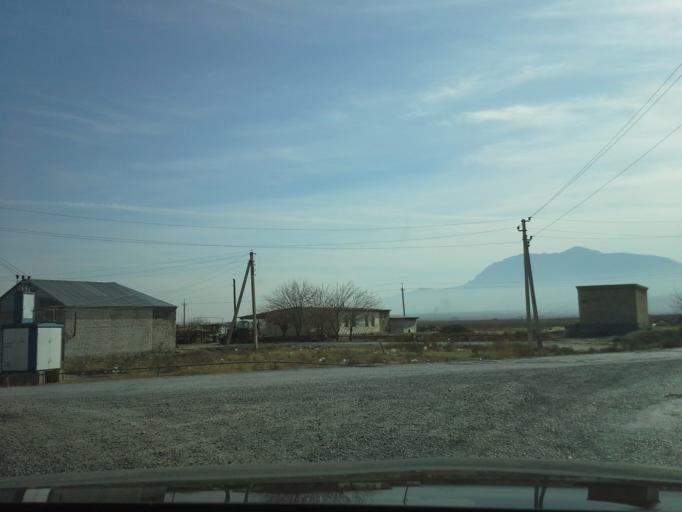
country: TM
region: Ahal
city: Arcabil
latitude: 38.1032
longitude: 57.9747
